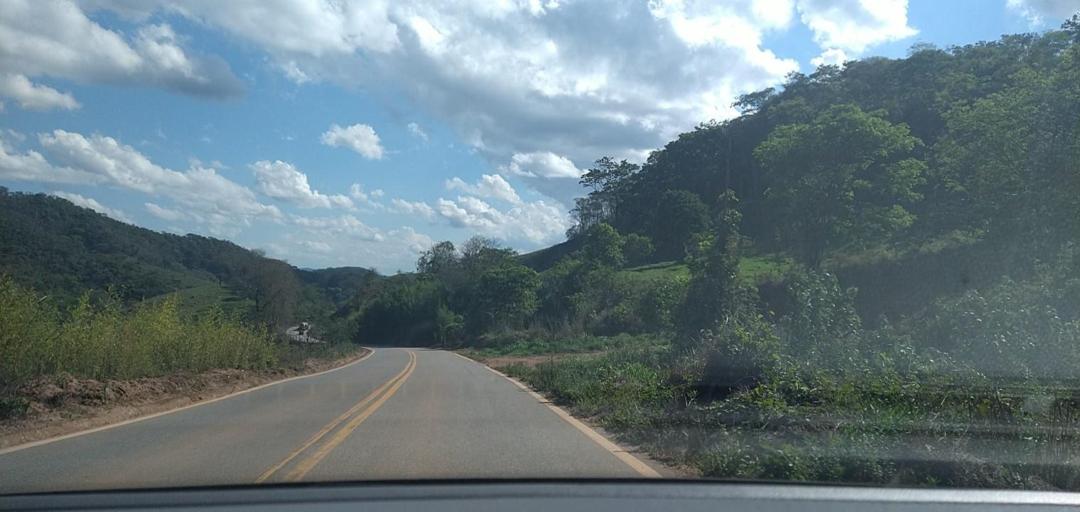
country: BR
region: Minas Gerais
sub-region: Alvinopolis
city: Alvinopolis
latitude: -20.0473
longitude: -43.0357
